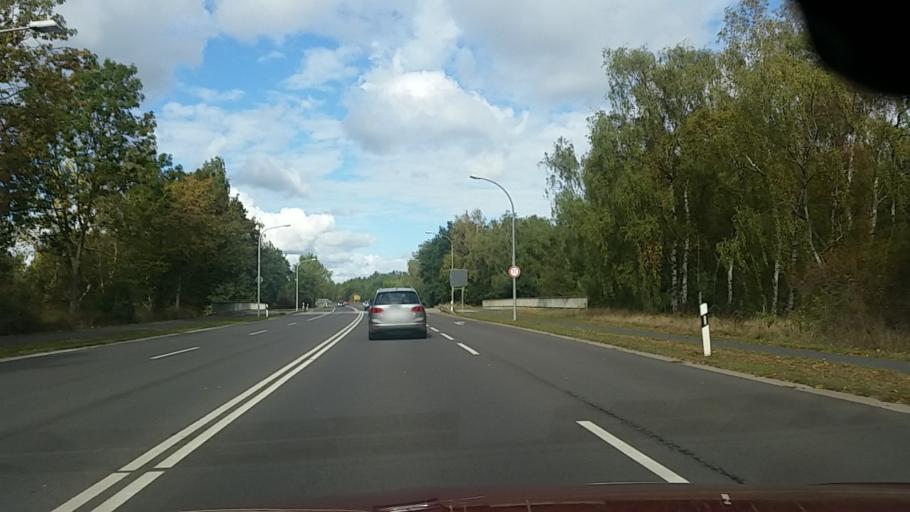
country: DE
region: Lower Saxony
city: Wolfsburg
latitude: 52.4412
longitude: 10.7939
